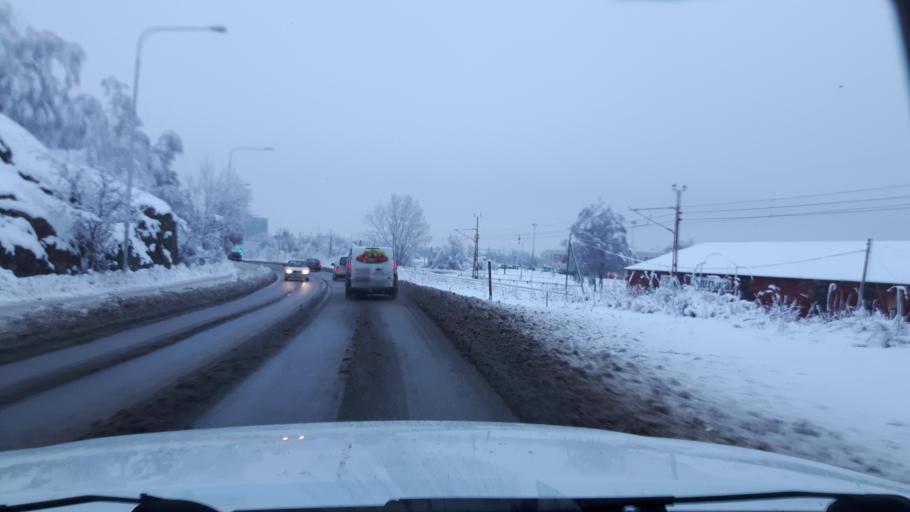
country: SE
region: Vaestra Goetaland
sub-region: Goteborg
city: Goeteborg
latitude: 57.7291
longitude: 11.9603
